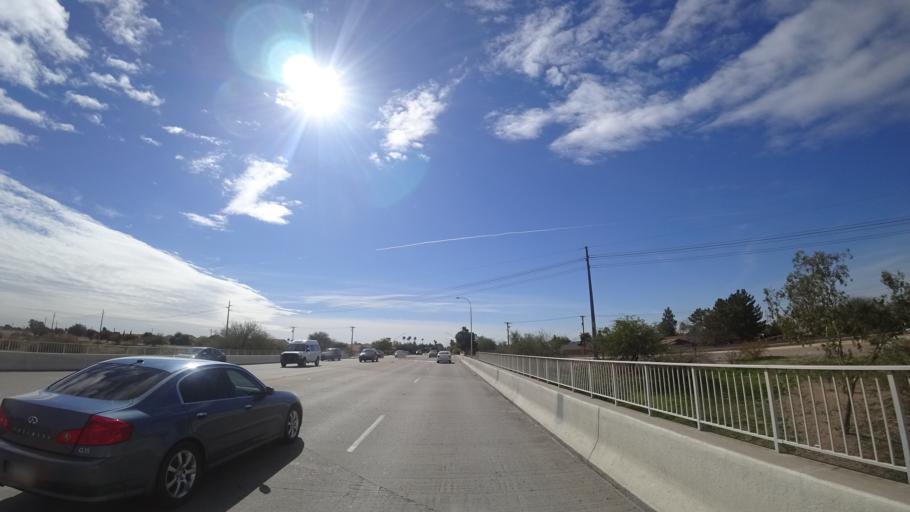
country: US
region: Arizona
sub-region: Maricopa County
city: Peoria
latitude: 33.6067
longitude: -112.1860
